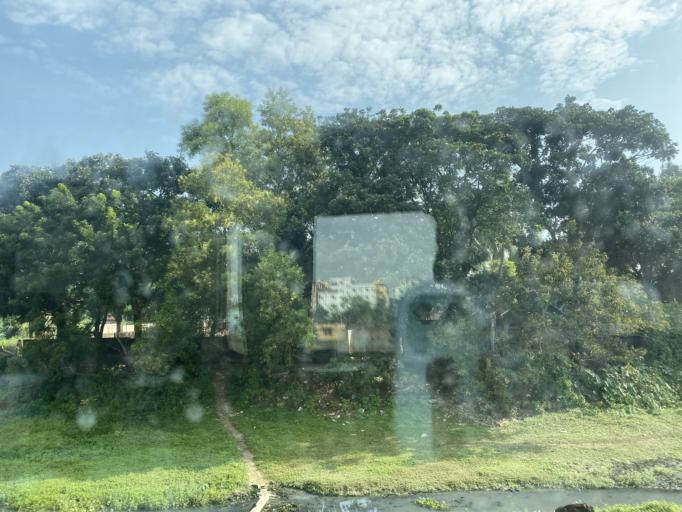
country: BD
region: Chittagong
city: Nabinagar
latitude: 23.9626
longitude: 91.1180
